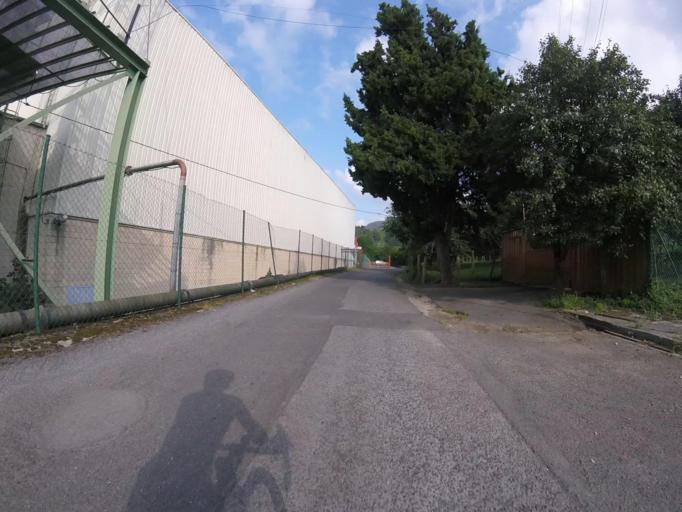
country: ES
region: Basque Country
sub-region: Provincia de Guipuzcoa
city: Astigarraga
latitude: 43.2584
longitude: -1.9503
